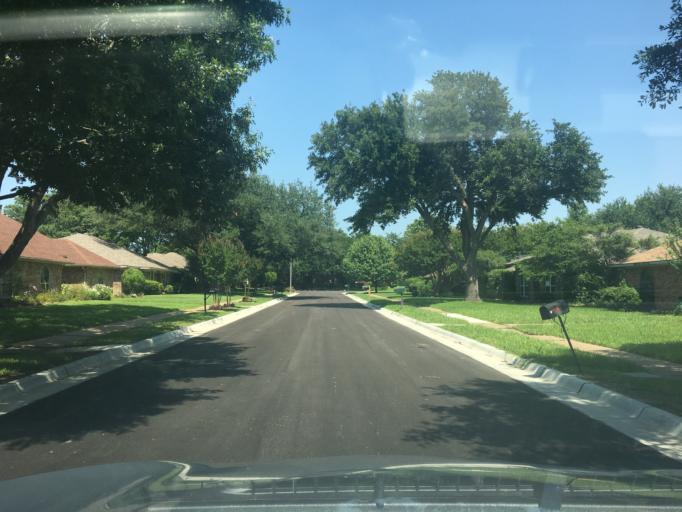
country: US
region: Texas
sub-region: Dallas County
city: Richardson
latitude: 32.9285
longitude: -96.7115
